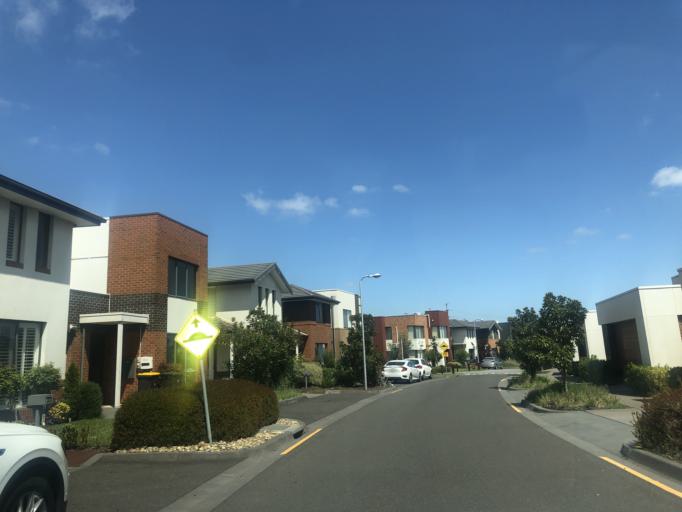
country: AU
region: Victoria
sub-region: Monash
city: Mulgrave
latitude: -37.9258
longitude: 145.1902
